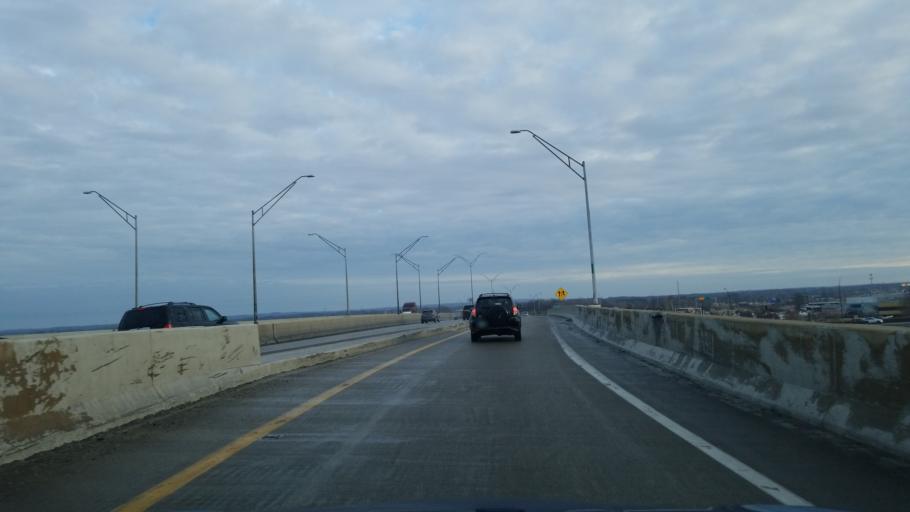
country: US
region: Ohio
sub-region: Cuyahoga County
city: Brook Park
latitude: 41.4226
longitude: -81.8207
